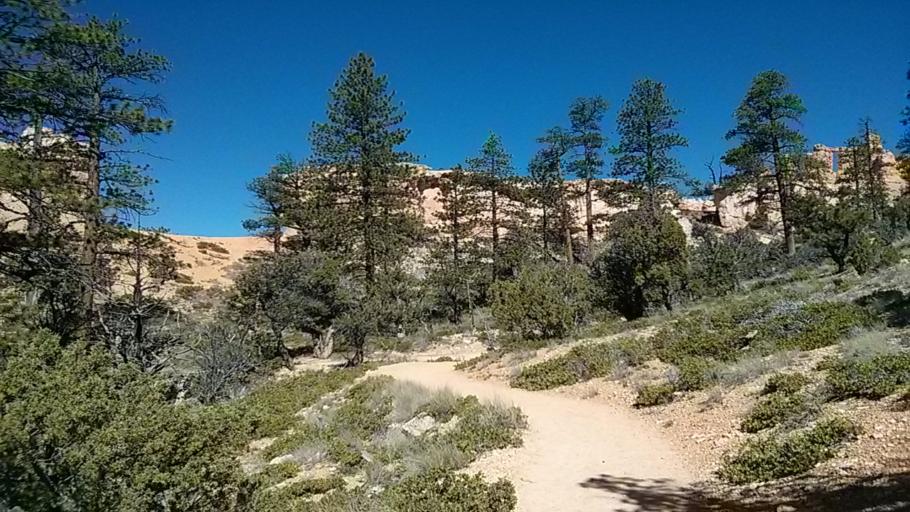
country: US
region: Utah
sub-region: Garfield County
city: Panguitch
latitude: 37.6357
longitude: -112.1439
